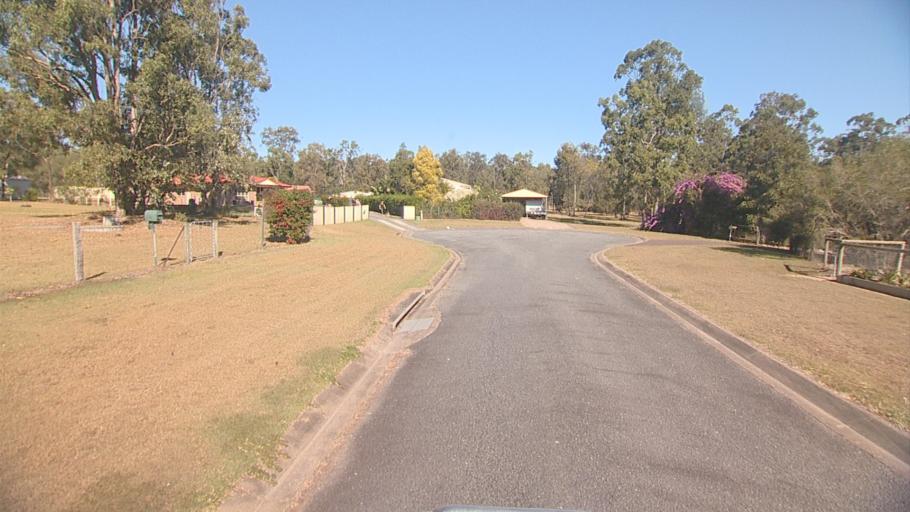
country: AU
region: Queensland
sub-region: Logan
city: North Maclean
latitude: -27.8210
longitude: 152.9499
